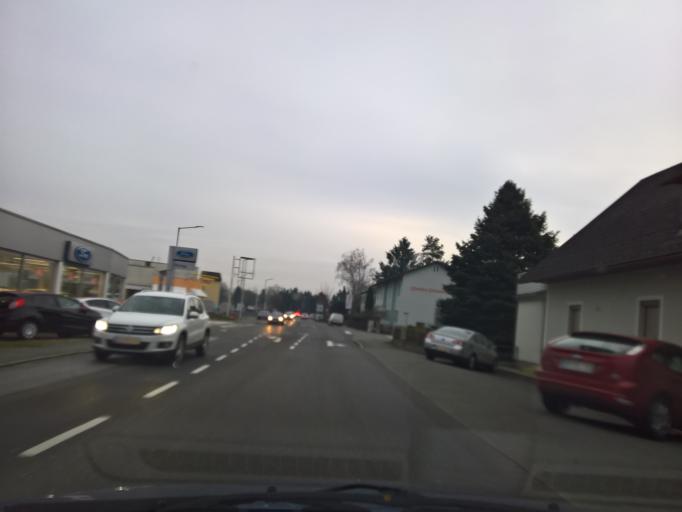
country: AT
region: Styria
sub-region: Politischer Bezirk Leibnitz
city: Gabersdorf
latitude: 46.7689
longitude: 15.5678
